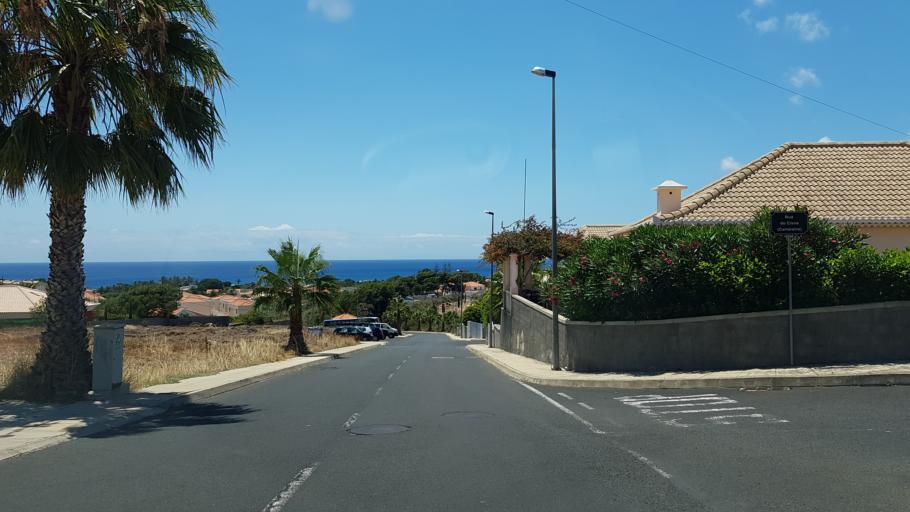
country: PT
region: Madeira
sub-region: Porto Santo
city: Vila de Porto Santo
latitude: 33.0559
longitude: -16.3527
